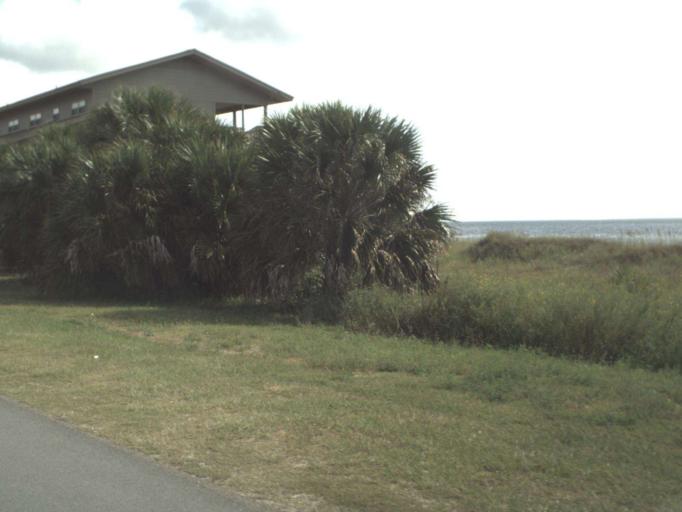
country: US
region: Florida
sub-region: Bay County
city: Mexico Beach
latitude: 29.8999
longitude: -85.3640
